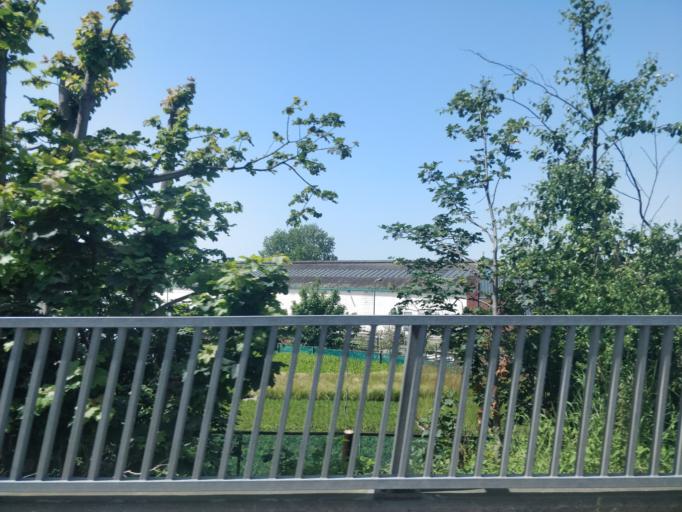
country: GB
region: England
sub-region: Lancashire
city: Banks
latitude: 53.6659
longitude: -2.9523
